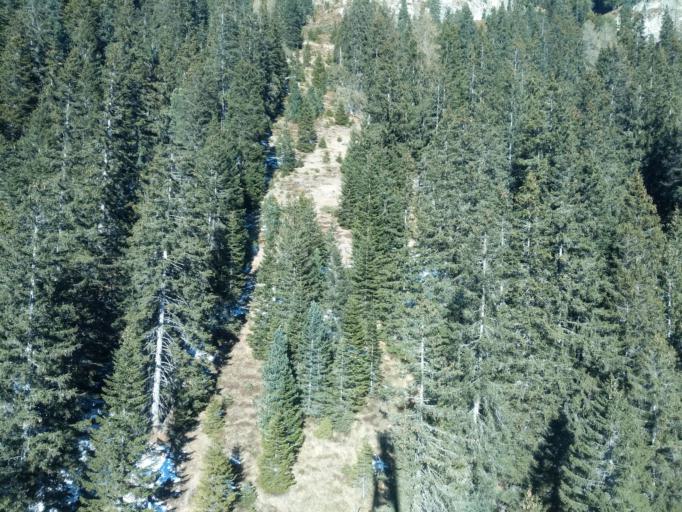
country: IT
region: Trentino-Alto Adige
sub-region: Provincia di Trento
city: Vigo di Fassa
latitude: 46.4307
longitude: 11.6667
